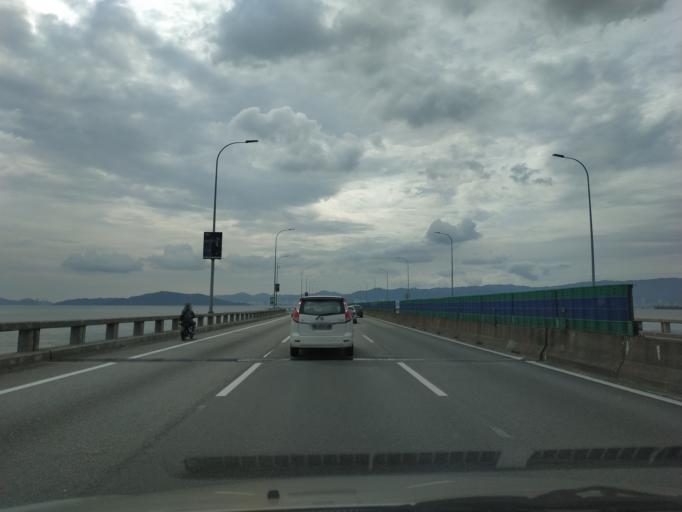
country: MY
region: Penang
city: Perai
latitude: 5.3531
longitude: 100.3869
